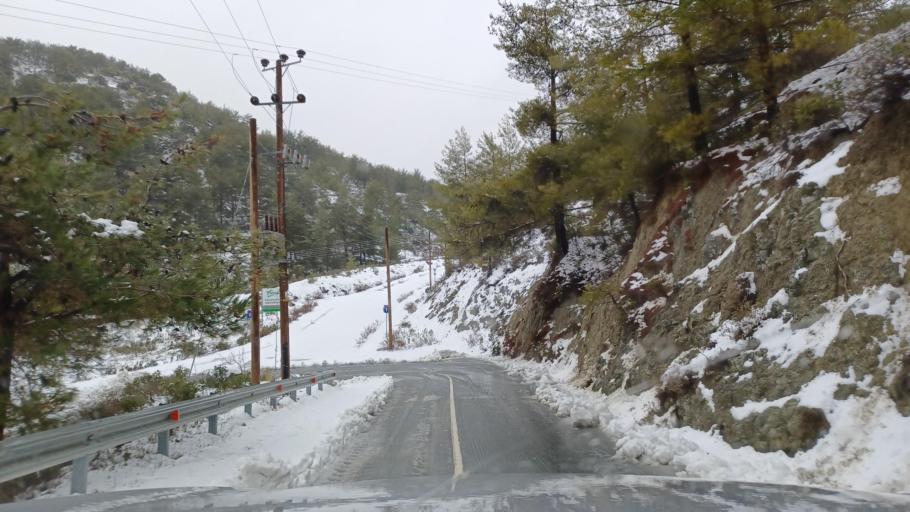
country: CY
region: Limassol
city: Pelendri
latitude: 34.9047
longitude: 32.9629
